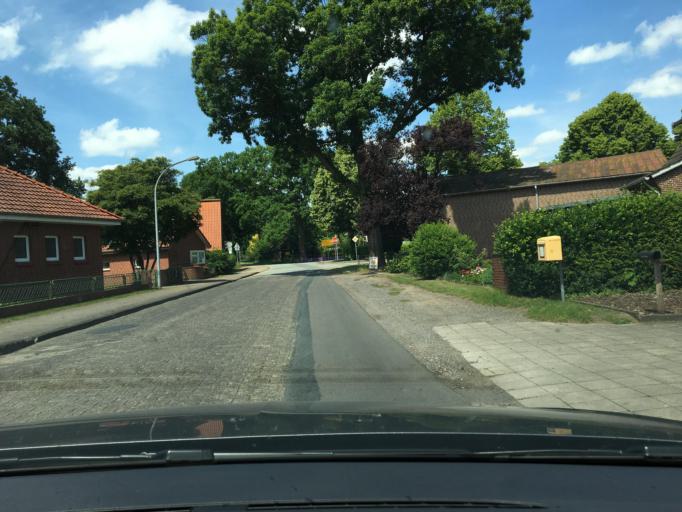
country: DE
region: Lower Saxony
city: Kirchtimke
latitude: 53.2573
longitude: 9.1843
